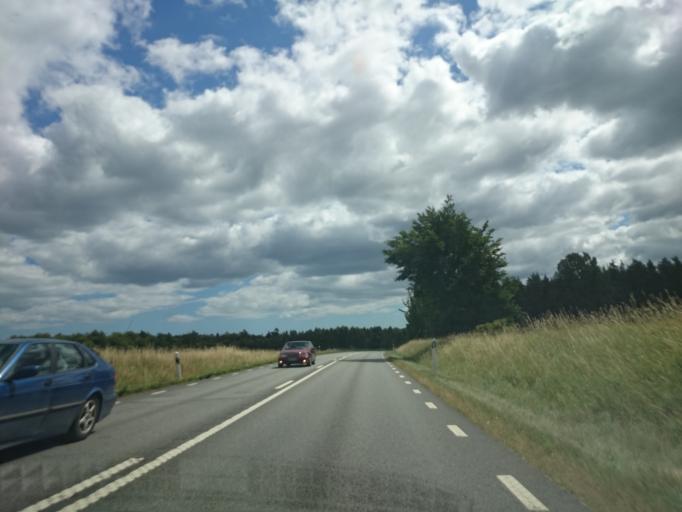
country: SE
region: Skane
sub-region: Kristianstads Kommun
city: Degeberga
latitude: 55.8182
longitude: 14.1266
